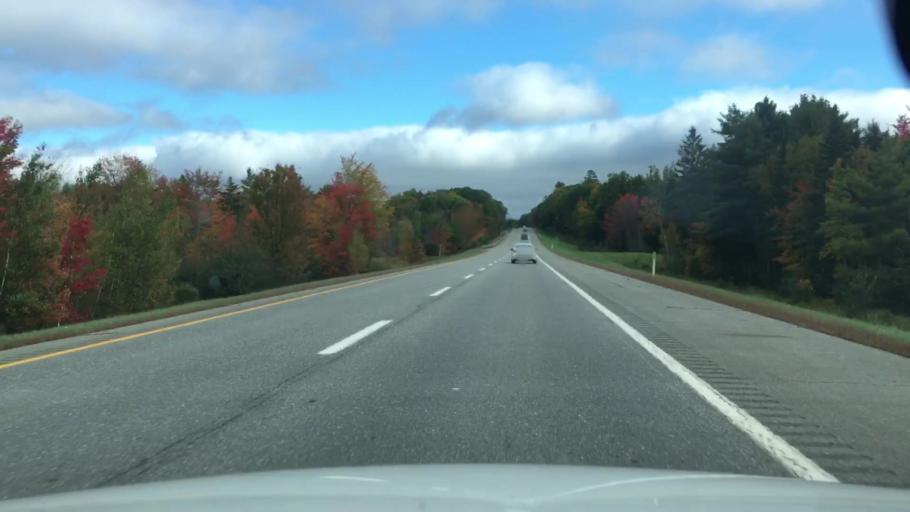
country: US
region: Maine
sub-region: Penobscot County
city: Carmel
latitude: 44.7641
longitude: -68.9903
